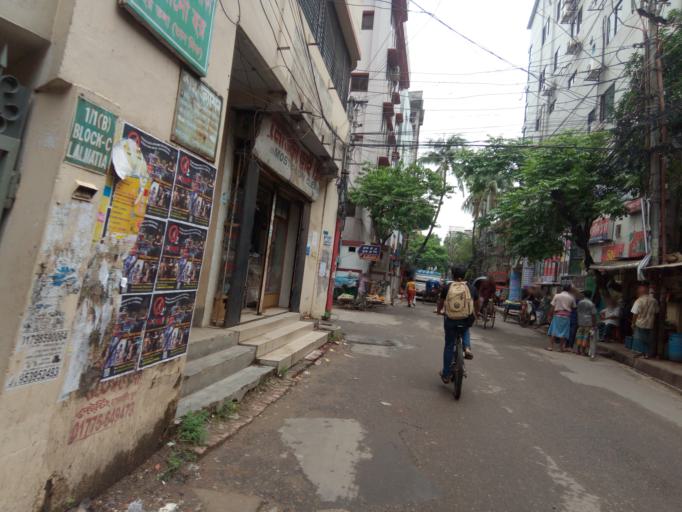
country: BD
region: Dhaka
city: Azimpur
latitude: 23.7555
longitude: 90.3726
